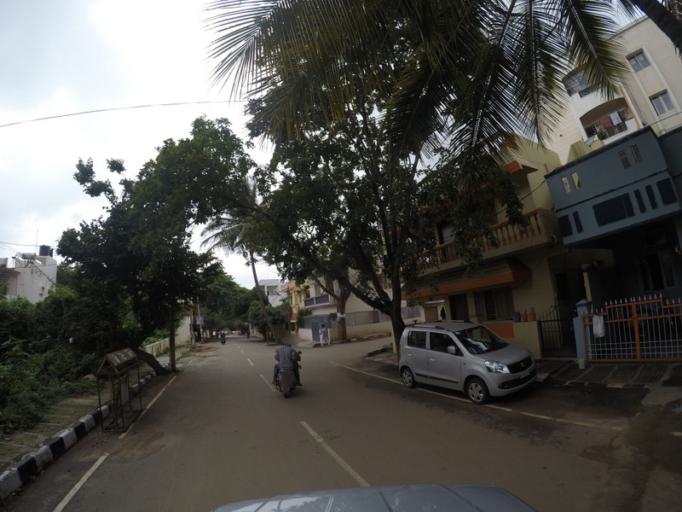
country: IN
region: Karnataka
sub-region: Bangalore Urban
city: Yelahanka
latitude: 13.0795
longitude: 77.5555
